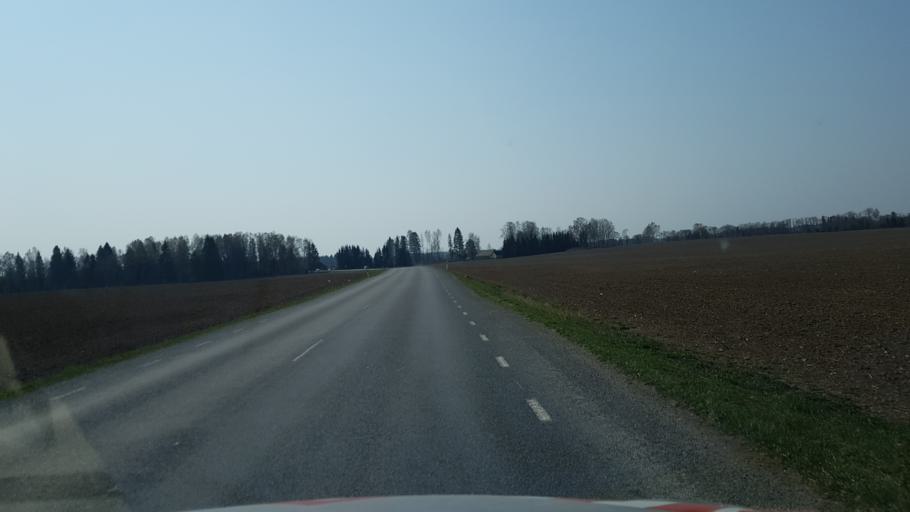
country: EE
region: Raplamaa
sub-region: Kehtna vald
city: Kehtna
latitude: 59.0167
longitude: 24.9224
